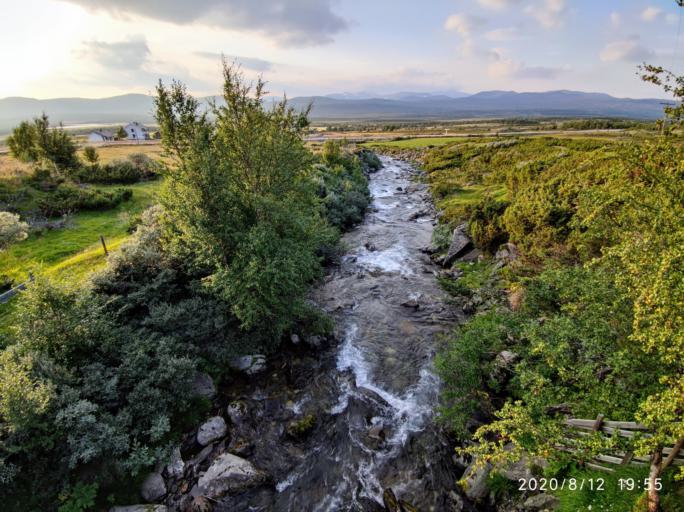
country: NO
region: Oppland
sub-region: Dovre
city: Dovre
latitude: 62.1123
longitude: 9.2901
